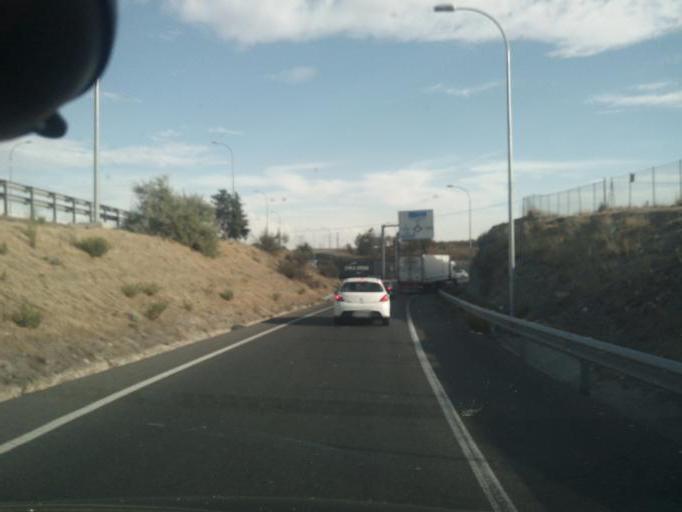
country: ES
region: Madrid
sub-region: Provincia de Madrid
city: Valdemoro
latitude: 40.1649
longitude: -3.6636
